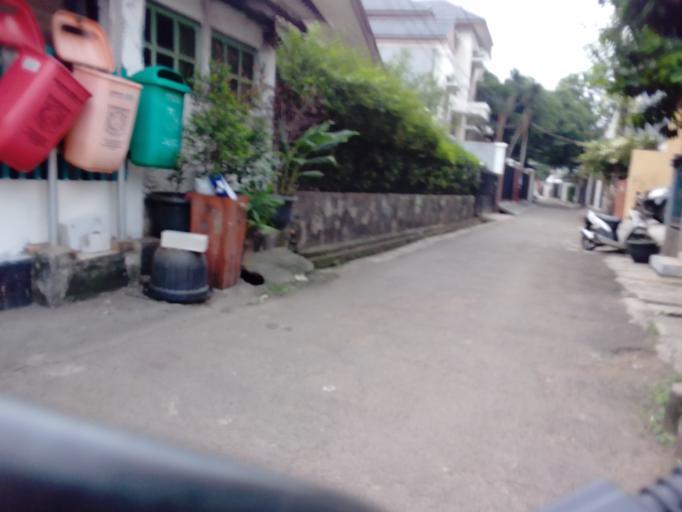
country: ID
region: Jakarta Raya
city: Jakarta
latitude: -6.2053
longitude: 106.8037
